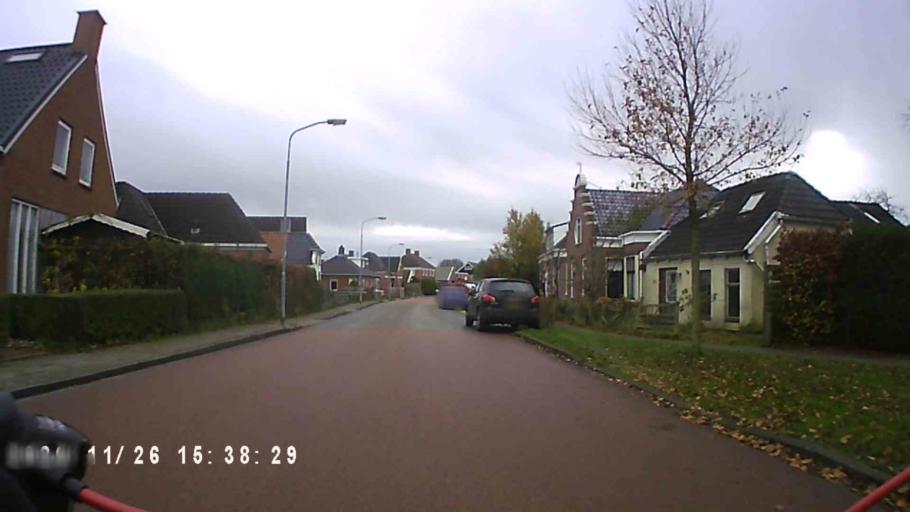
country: NL
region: Groningen
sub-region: Gemeente Slochteren
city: Slochteren
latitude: 53.2986
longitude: 6.7292
